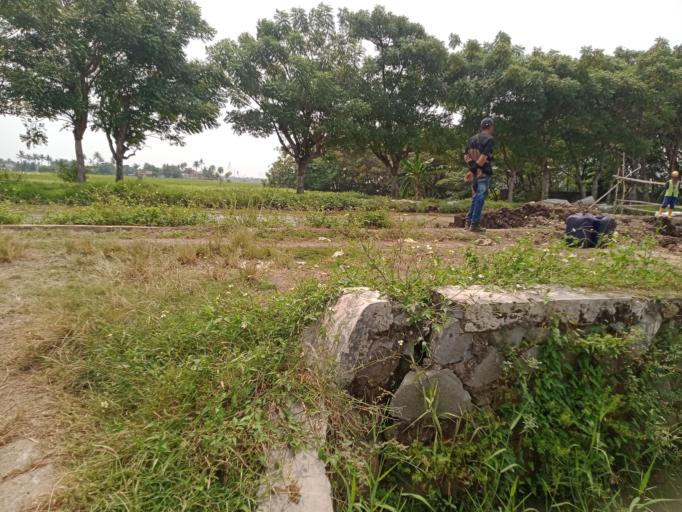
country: ID
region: West Java
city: Sepatan
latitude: -6.1017
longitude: 106.5727
